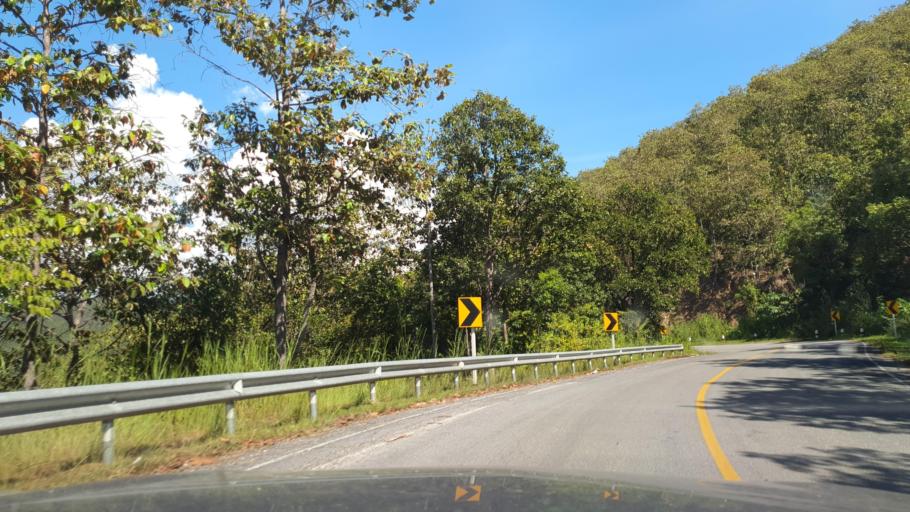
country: TH
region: Chiang Mai
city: Phrao
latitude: 19.3710
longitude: 99.2471
